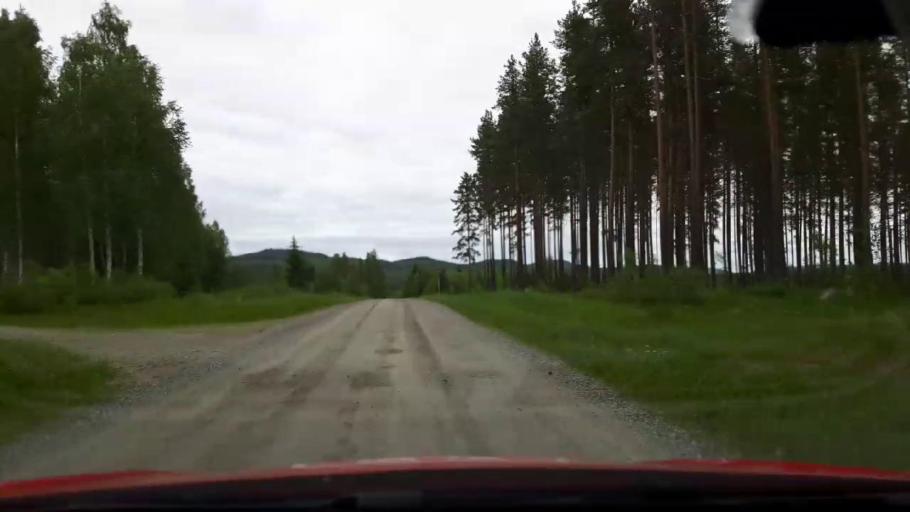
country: SE
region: Jaemtland
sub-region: Ragunda Kommun
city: Hammarstrand
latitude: 63.2133
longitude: 16.0765
